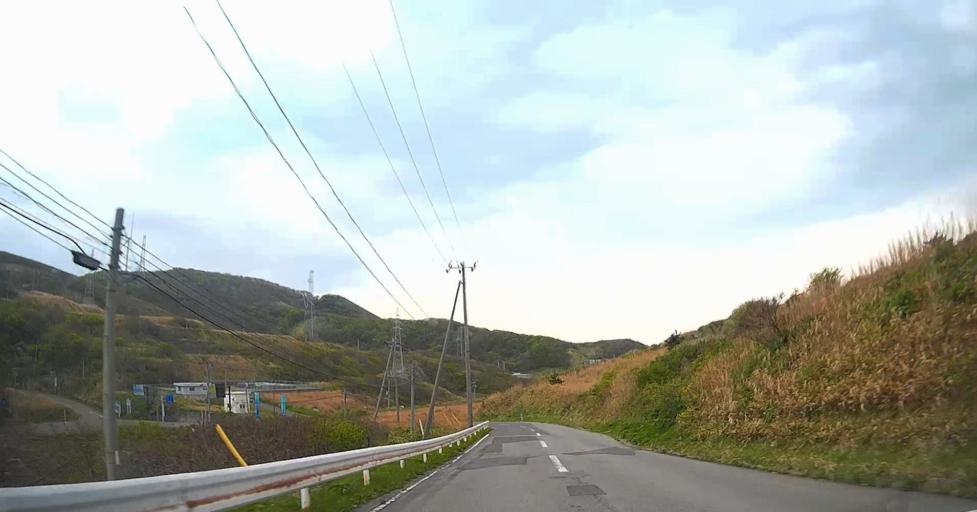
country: JP
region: Aomori
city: Shimokizukuri
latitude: 41.2555
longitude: 140.3493
